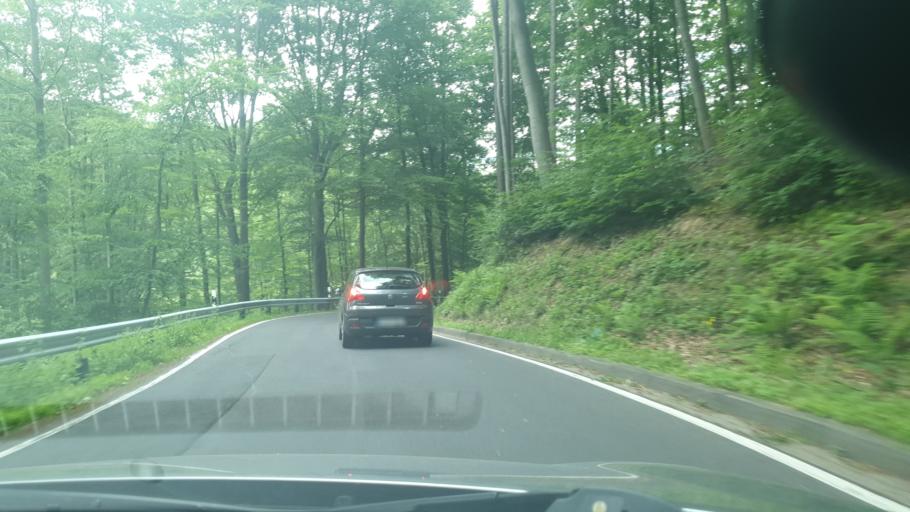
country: DE
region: Rheinland-Pfalz
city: Neuhausel
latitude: 50.3961
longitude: 7.7162
